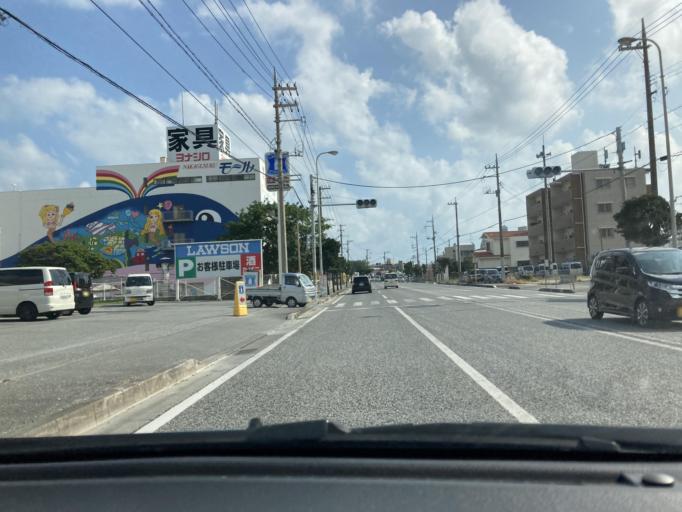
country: JP
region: Okinawa
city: Chatan
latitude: 26.2857
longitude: 127.8152
